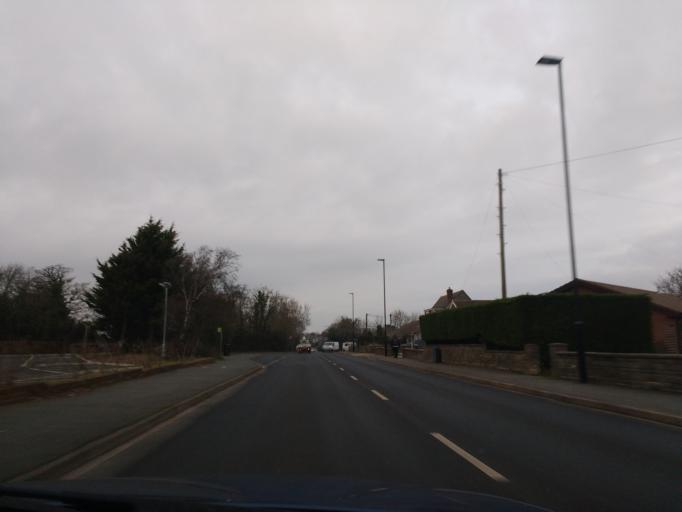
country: GB
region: England
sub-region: Isle of Wight
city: Northwood
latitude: 50.7485
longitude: -1.3123
